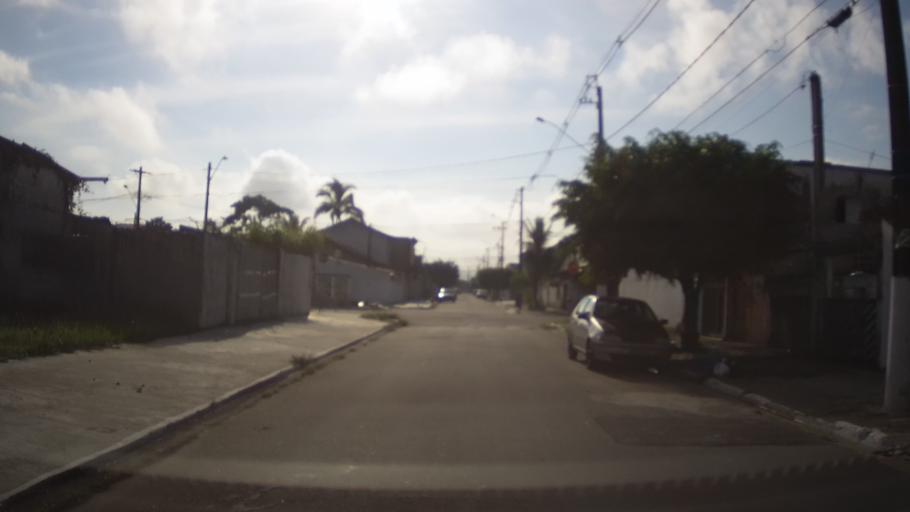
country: BR
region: Sao Paulo
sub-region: Praia Grande
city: Praia Grande
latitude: -24.0146
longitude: -46.4812
